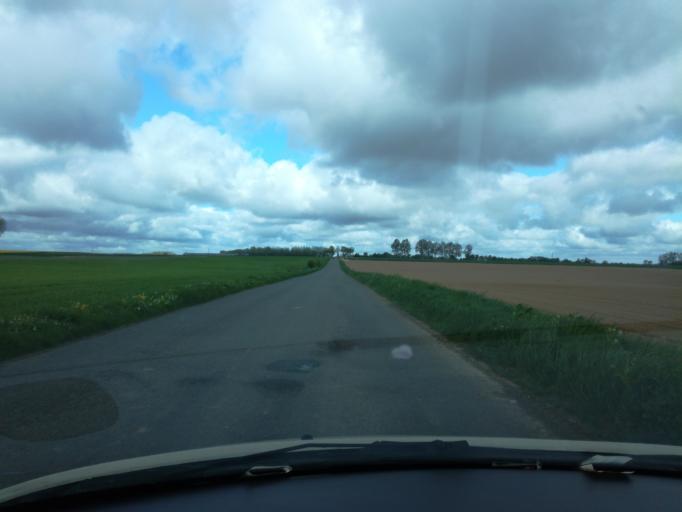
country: FR
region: Picardie
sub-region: Departement de la Somme
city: Poix-de-Picardie
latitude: 49.8196
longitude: 1.9630
